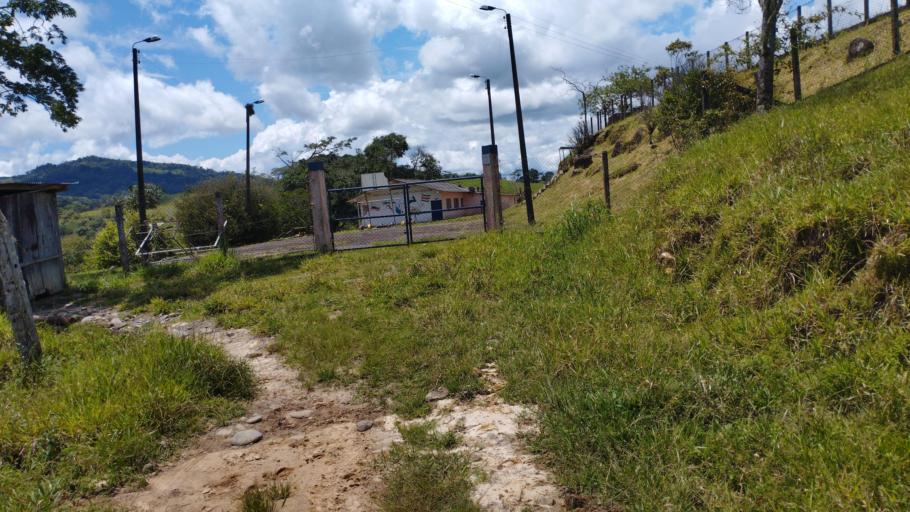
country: CO
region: Boyaca
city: San Luis de Gaceno
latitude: 4.7749
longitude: -73.1313
